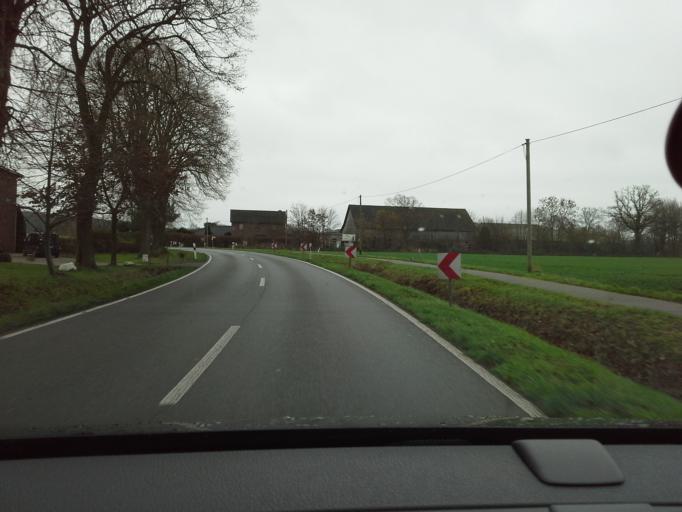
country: DE
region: Schleswig-Holstein
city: Bilsen
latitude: 53.7593
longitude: 9.8593
